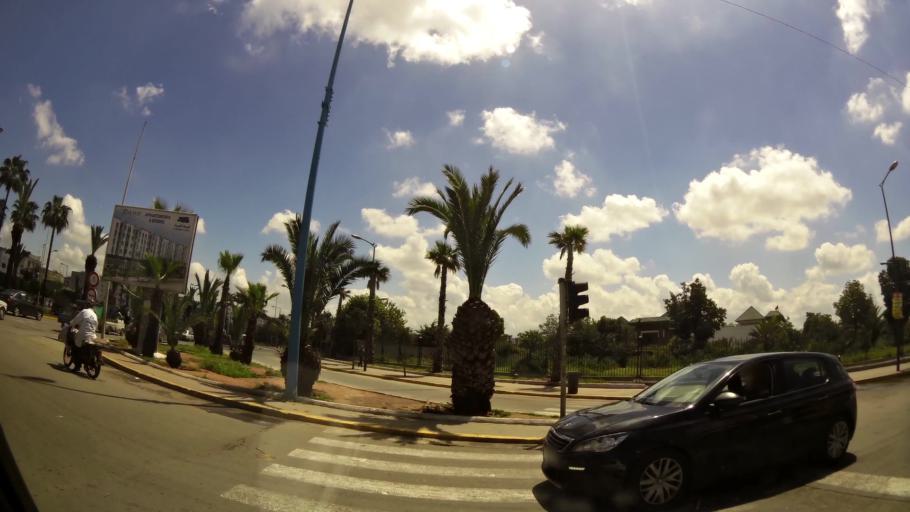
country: MA
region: Grand Casablanca
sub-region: Casablanca
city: Casablanca
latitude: 33.5606
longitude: -7.5649
